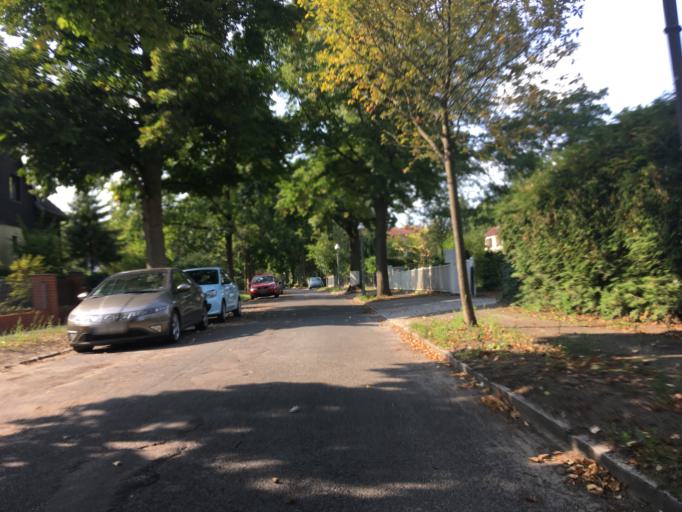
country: DE
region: Brandenburg
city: Glienicke
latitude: 52.6247
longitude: 13.3289
